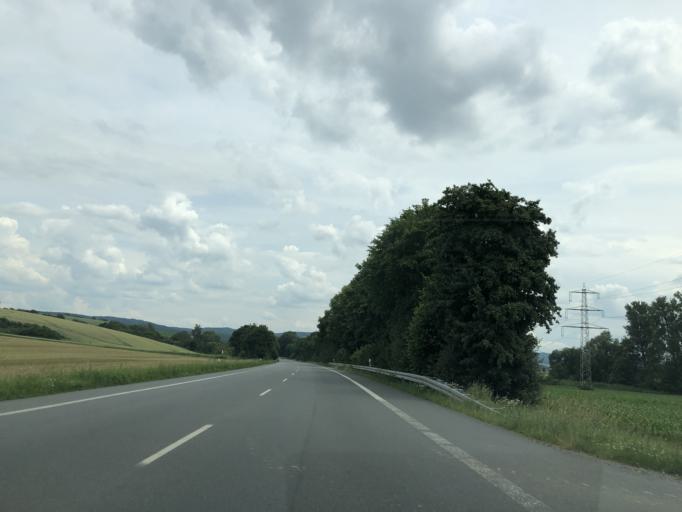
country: DE
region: Hesse
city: Gross-Bieberau
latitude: 49.7906
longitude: 8.8471
